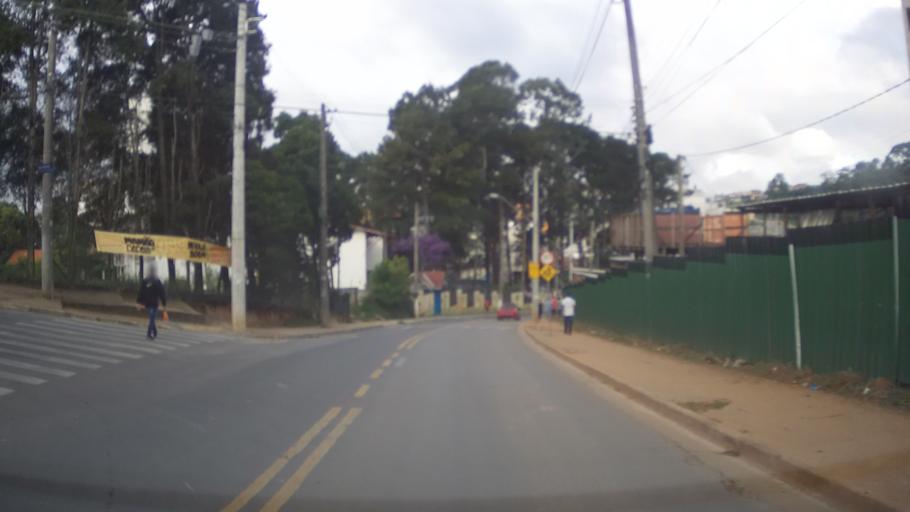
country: BR
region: Sao Paulo
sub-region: Itaquaquecetuba
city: Itaquaquecetuba
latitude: -23.4543
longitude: -46.4302
